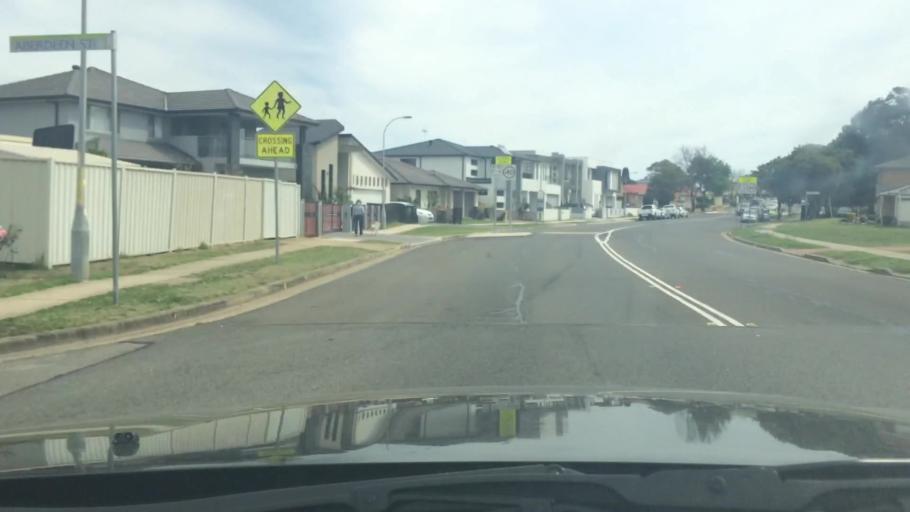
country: AU
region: New South Wales
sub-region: Fairfield
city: Cabramatta West
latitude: -33.8674
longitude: 150.8932
